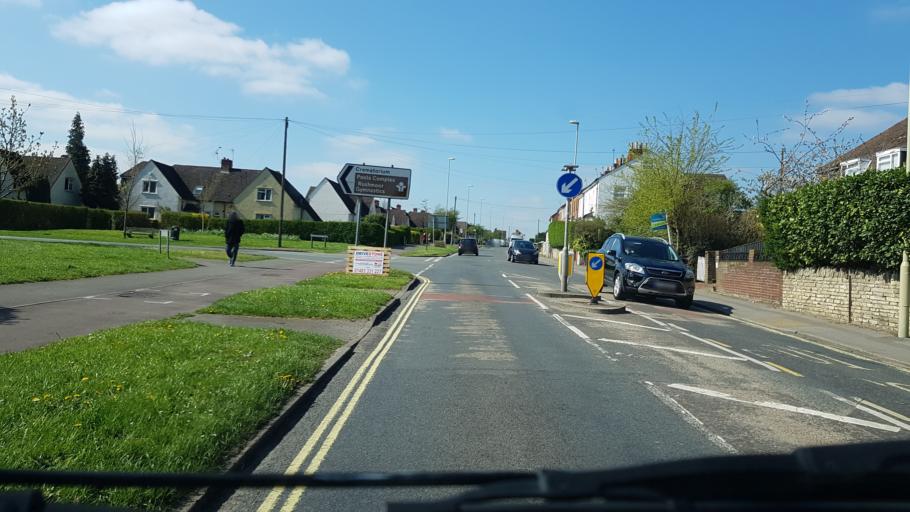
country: GB
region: England
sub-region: Hampshire
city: Aldershot
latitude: 51.2385
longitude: -0.7478
